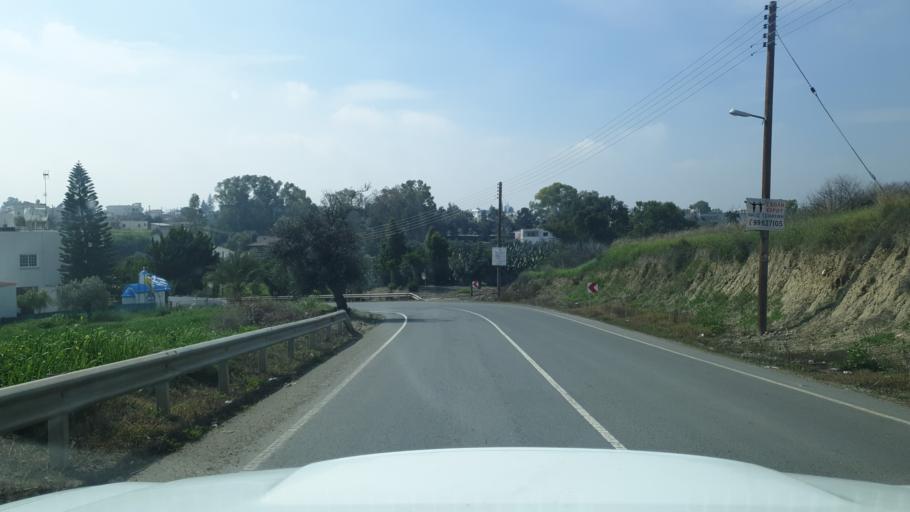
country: CY
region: Lefkosia
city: Kato Deftera
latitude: 35.0897
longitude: 33.2781
